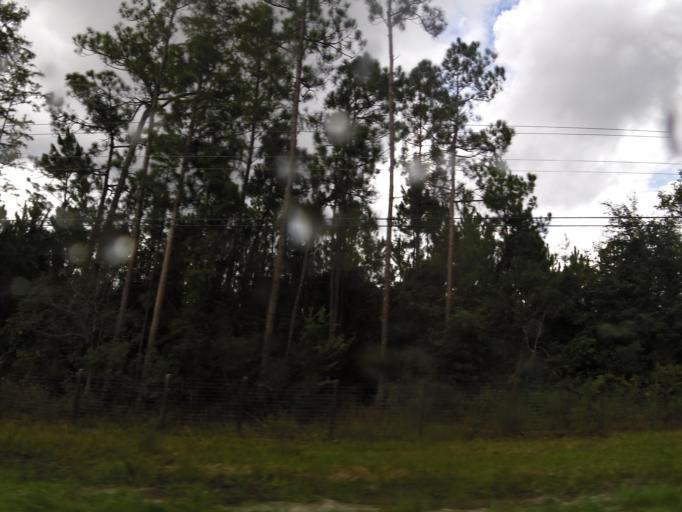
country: US
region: Florida
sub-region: Clay County
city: Asbury Lake
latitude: 30.0374
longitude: -81.8316
